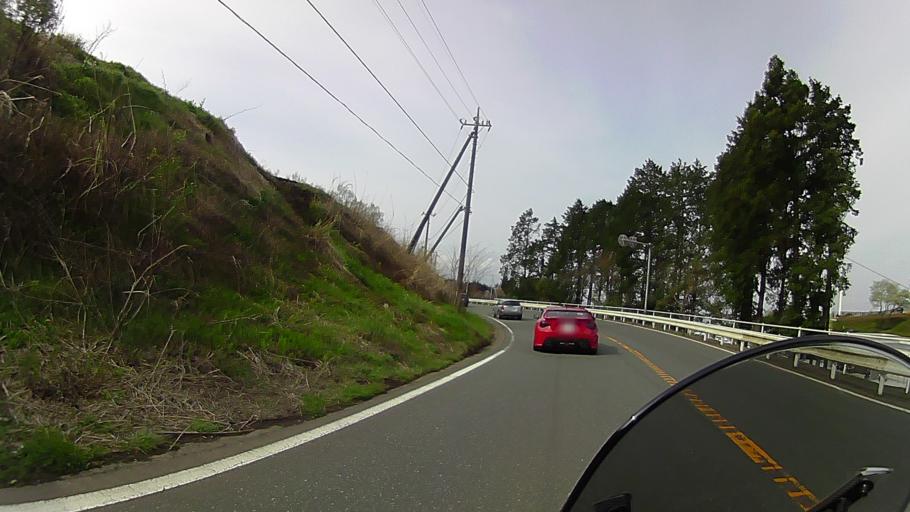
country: JP
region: Kanagawa
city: Hakone
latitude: 35.1504
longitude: 138.9841
